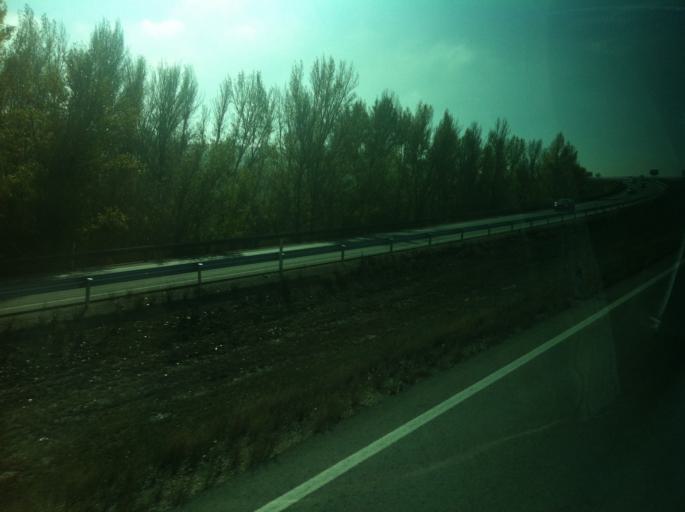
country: ES
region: Castille and Leon
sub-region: Provincia de Burgos
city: Rubena
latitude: 42.3888
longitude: -3.5799
